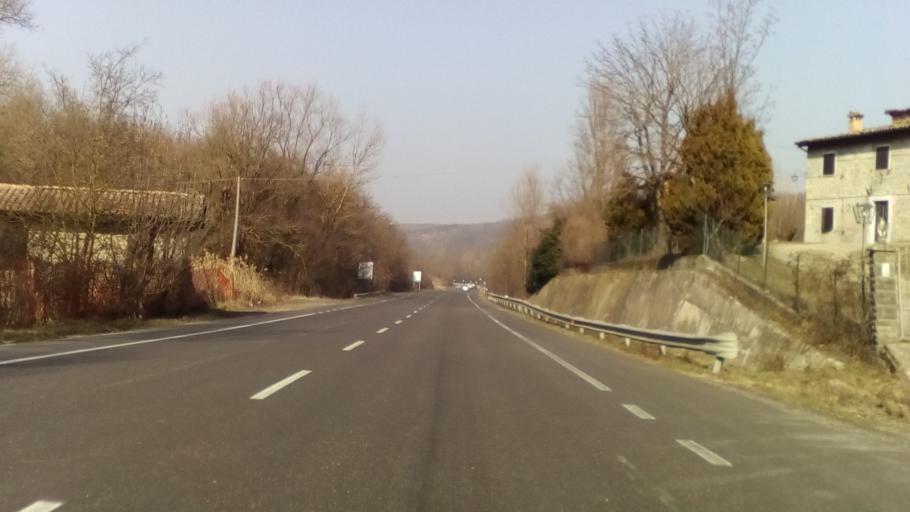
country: IT
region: Emilia-Romagna
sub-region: Provincia di Modena
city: Serramazzoni
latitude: 44.4396
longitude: 10.8340
